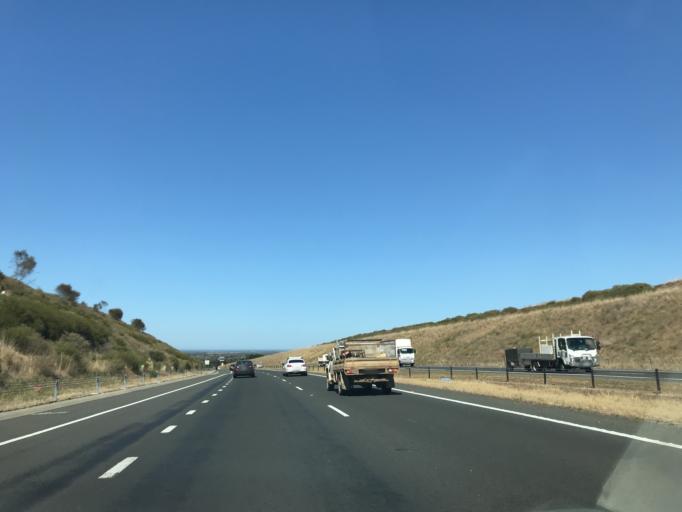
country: AU
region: Victoria
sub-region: Greater Geelong
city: Wandana Heights
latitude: -38.1758
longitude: 144.2942
